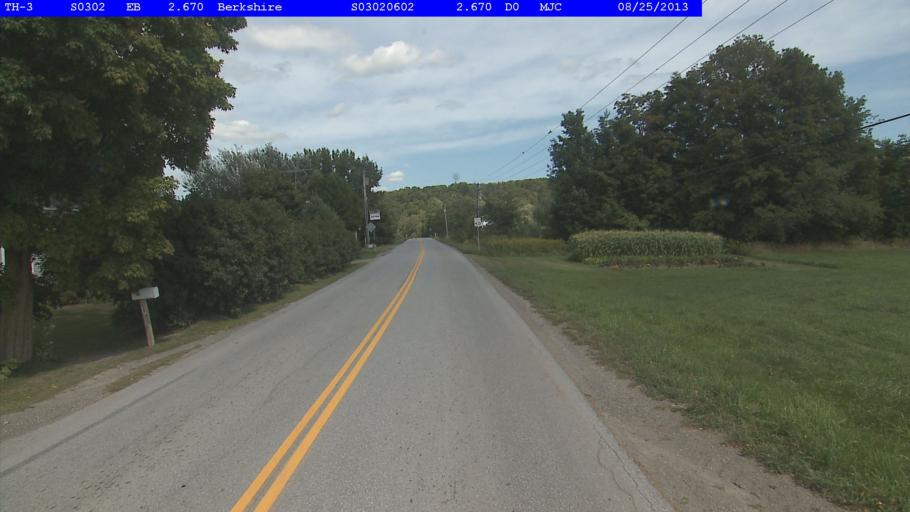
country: US
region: Vermont
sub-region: Franklin County
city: Enosburg Falls
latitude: 44.9733
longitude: -72.7656
